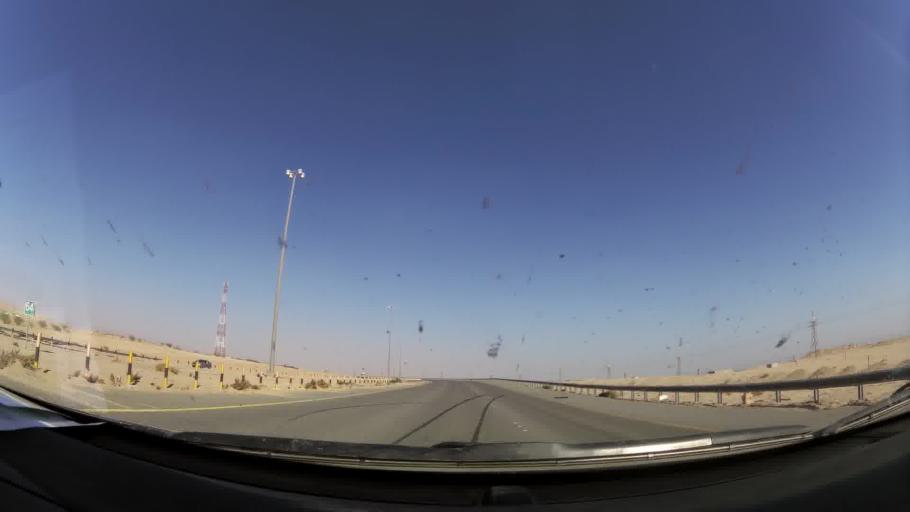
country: KW
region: Muhafazat al Jahra'
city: Al Jahra'
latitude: 29.4469
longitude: 47.7529
